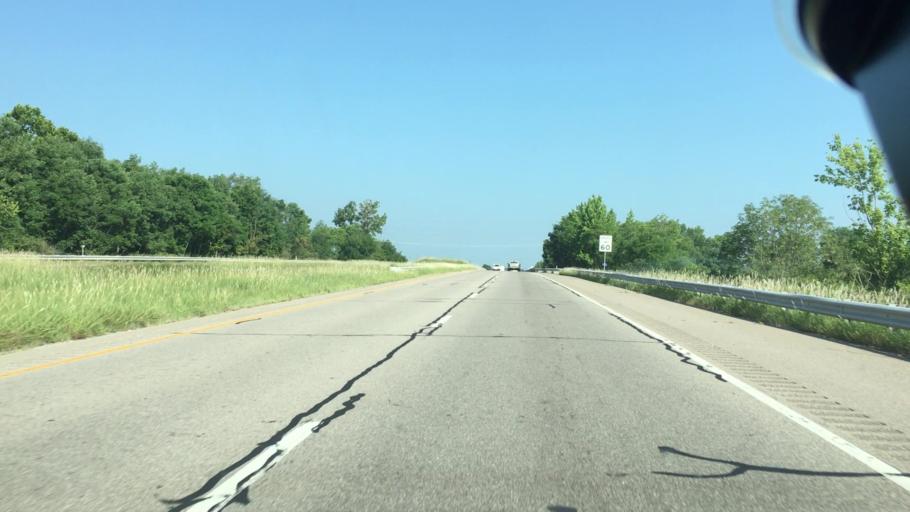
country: US
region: Indiana
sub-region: Gibson County
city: Princeton
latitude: 38.3188
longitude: -87.5736
